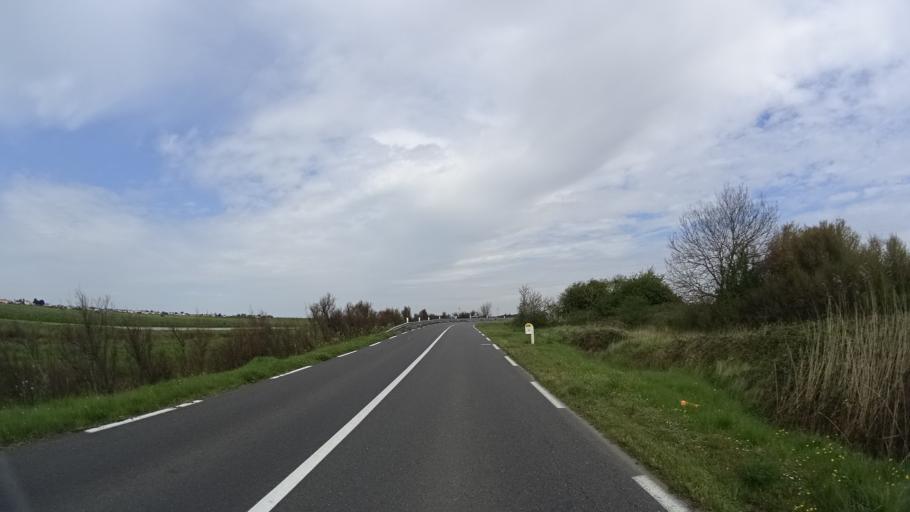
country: FR
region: Pays de la Loire
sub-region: Departement de la Vendee
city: Beauvoir-sur-Mer
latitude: 46.9257
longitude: -2.0405
